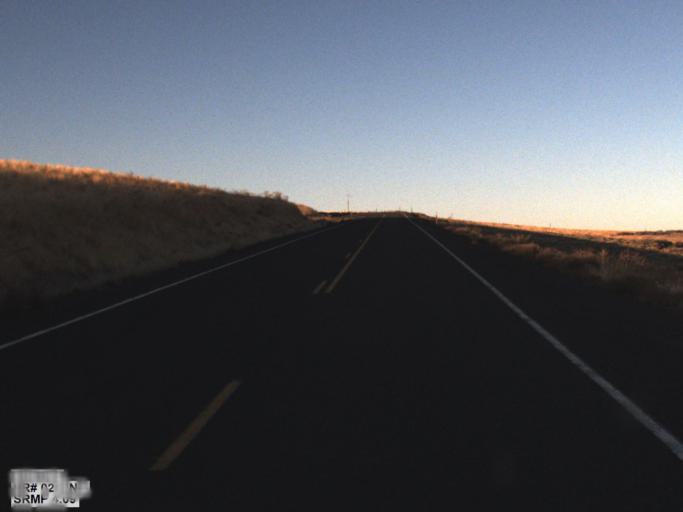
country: US
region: Washington
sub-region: Franklin County
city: Connell
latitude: 46.6963
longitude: -118.5284
